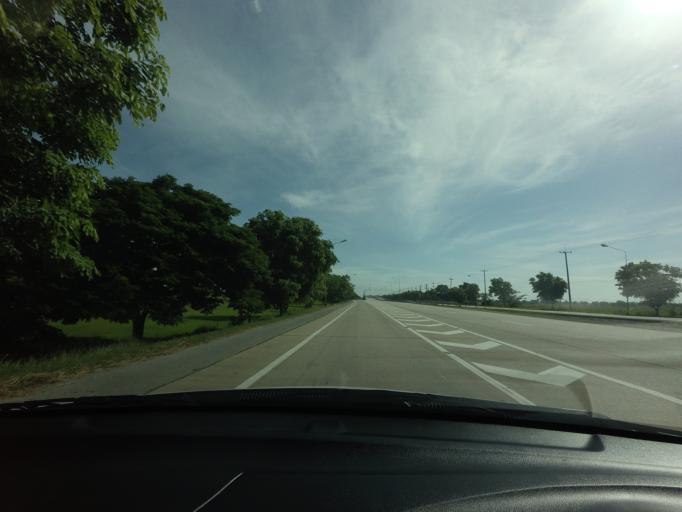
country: TH
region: Suphan Buri
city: Suphan Buri
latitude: 14.4943
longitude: 100.0460
